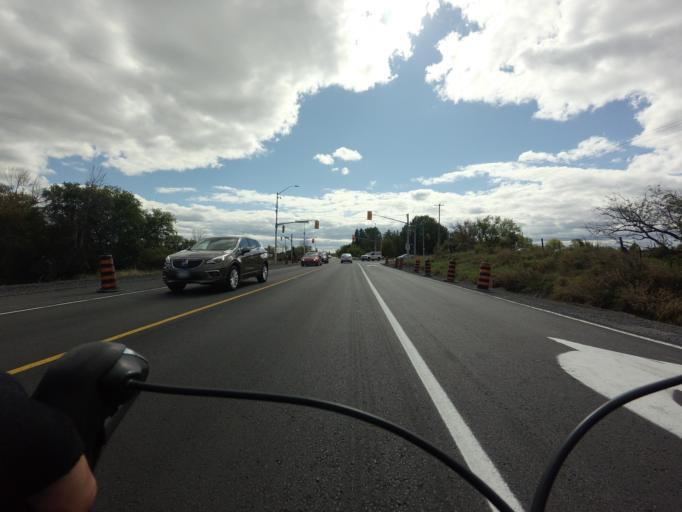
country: CA
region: Ontario
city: Ottawa
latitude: 45.3101
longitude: -75.7017
